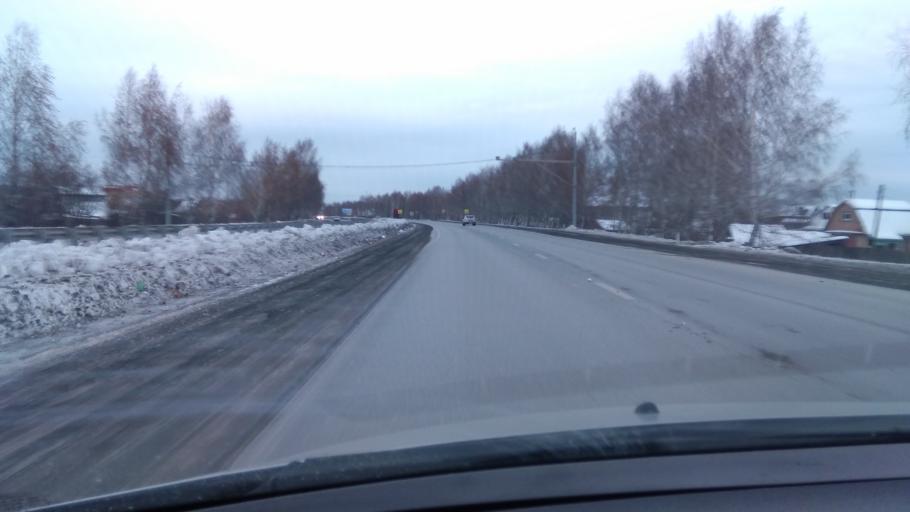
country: RU
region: Sverdlovsk
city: Aramil
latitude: 56.7009
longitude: 60.7493
